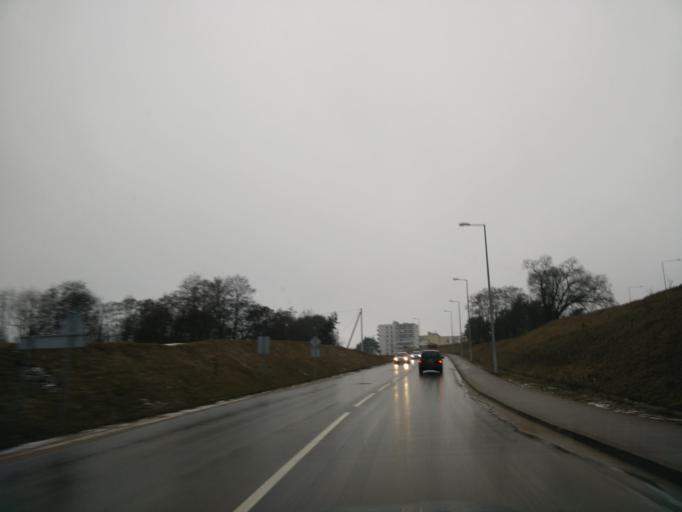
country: LT
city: Grigiskes
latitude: 54.6684
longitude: 25.1084
